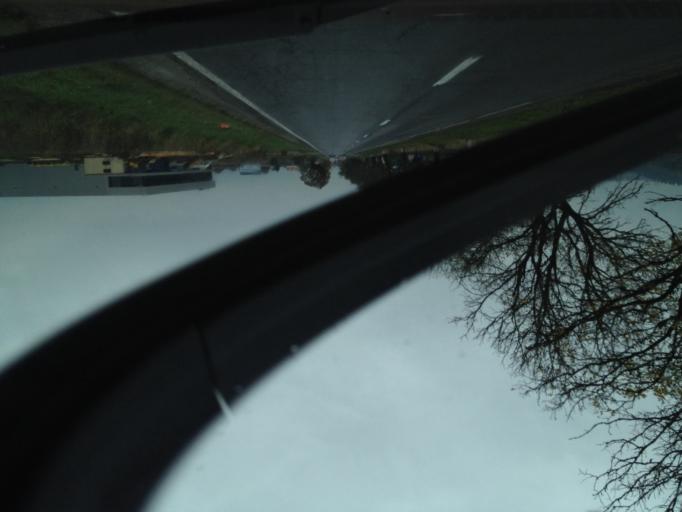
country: RO
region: Brasov
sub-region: Comuna Ghimbav
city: Ghimbav
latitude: 45.6372
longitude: 25.5005
